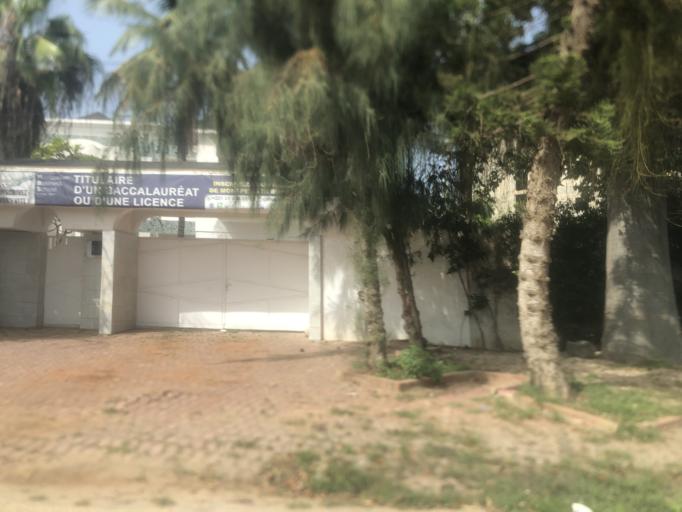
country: SN
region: Dakar
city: Mermoz Boabab
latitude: 14.7375
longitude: -17.5109
